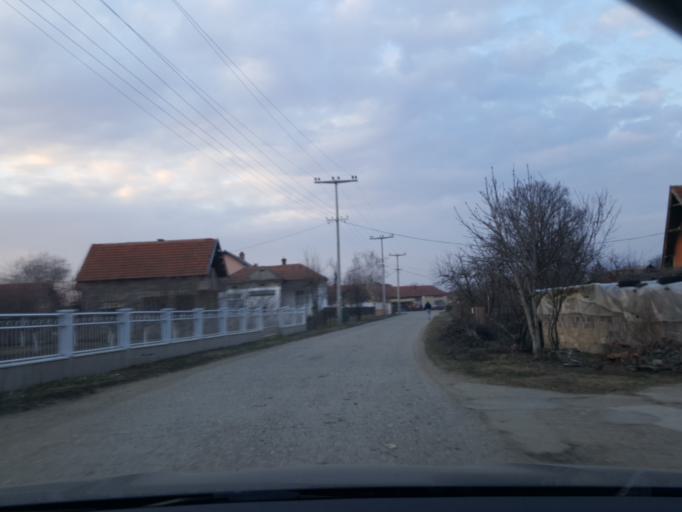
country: RS
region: Central Serbia
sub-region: Nisavski Okrug
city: Aleksinac
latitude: 43.5604
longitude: 21.6471
